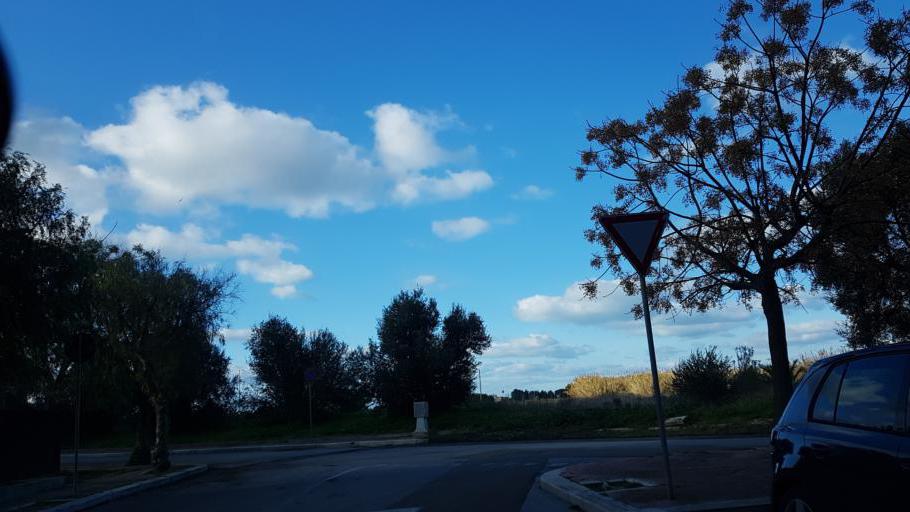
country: IT
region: Apulia
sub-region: Provincia di Brindisi
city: Brindisi
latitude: 40.6512
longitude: 17.9212
